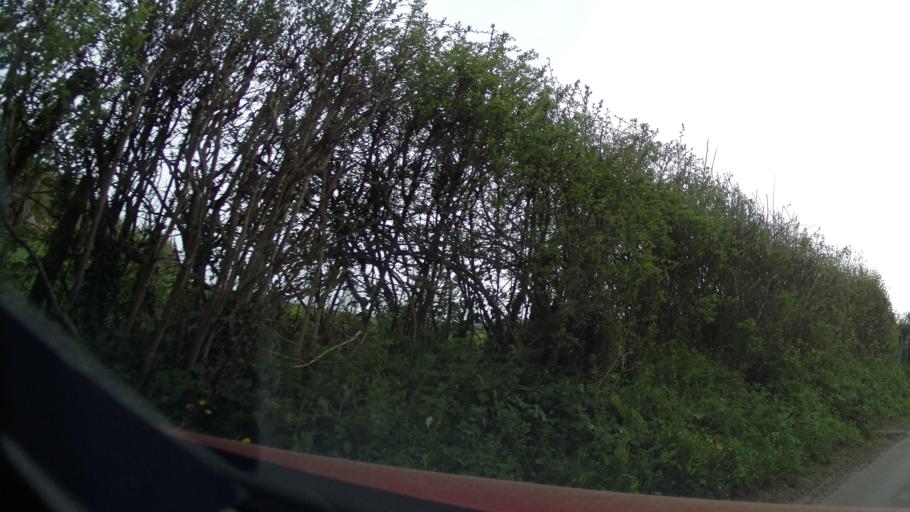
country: GB
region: England
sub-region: Somerset
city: Milborne Port
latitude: 50.9487
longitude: -2.4612
